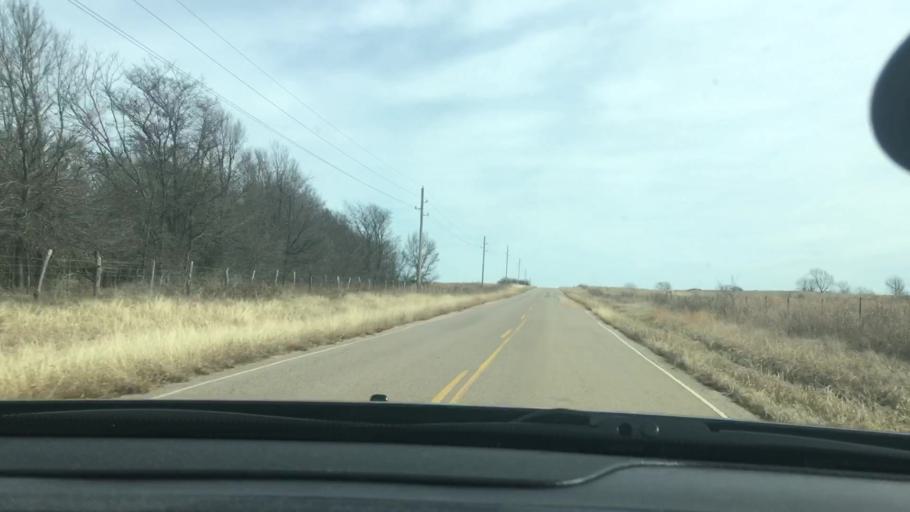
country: US
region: Oklahoma
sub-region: Murray County
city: Sulphur
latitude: 34.4049
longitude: -96.8959
